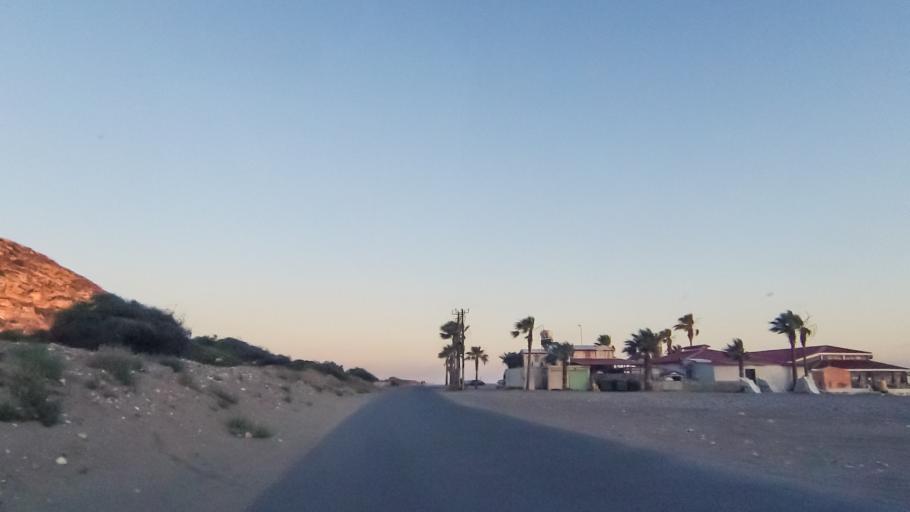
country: CY
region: Limassol
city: Erimi
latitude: 34.6640
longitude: 32.8814
